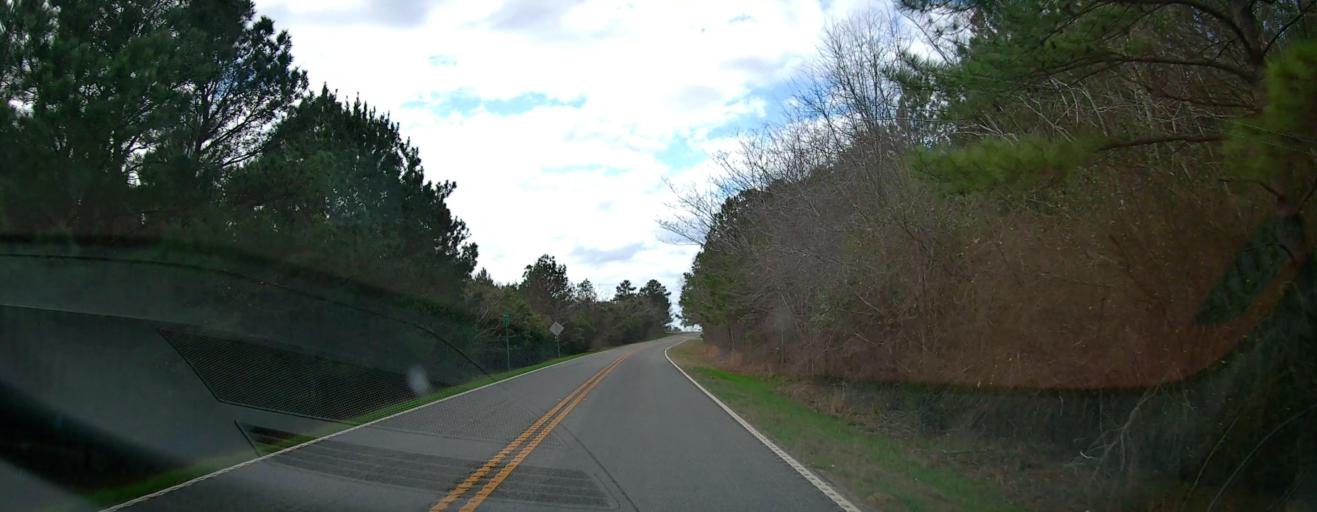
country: US
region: Georgia
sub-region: Marion County
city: Buena Vista
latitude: 32.4344
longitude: -84.4302
